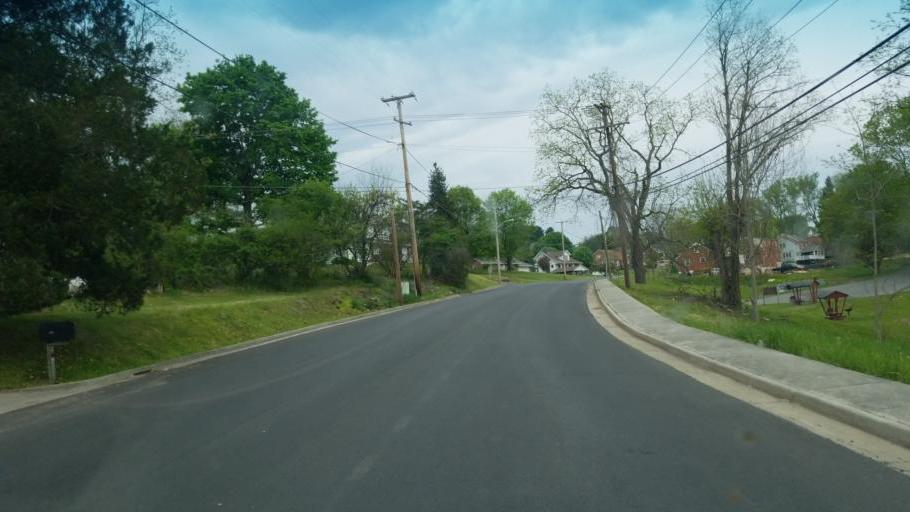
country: US
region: Virginia
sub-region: Smyth County
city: Marion
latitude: 36.8401
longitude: -81.5183
